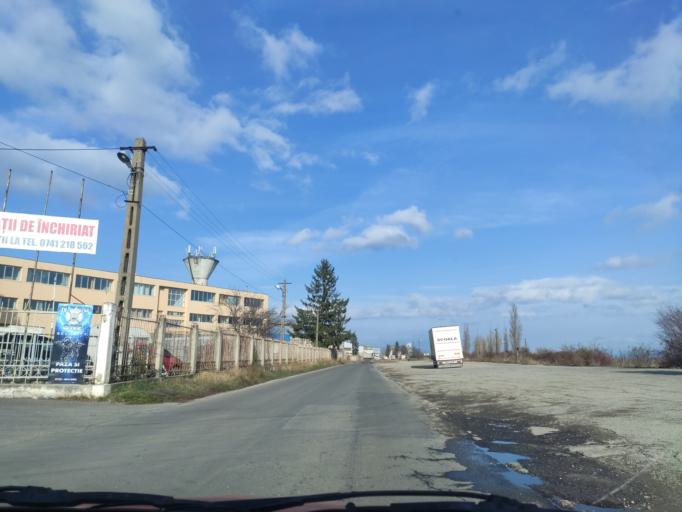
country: RO
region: Brasov
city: Codlea
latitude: 45.6888
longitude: 25.4567
